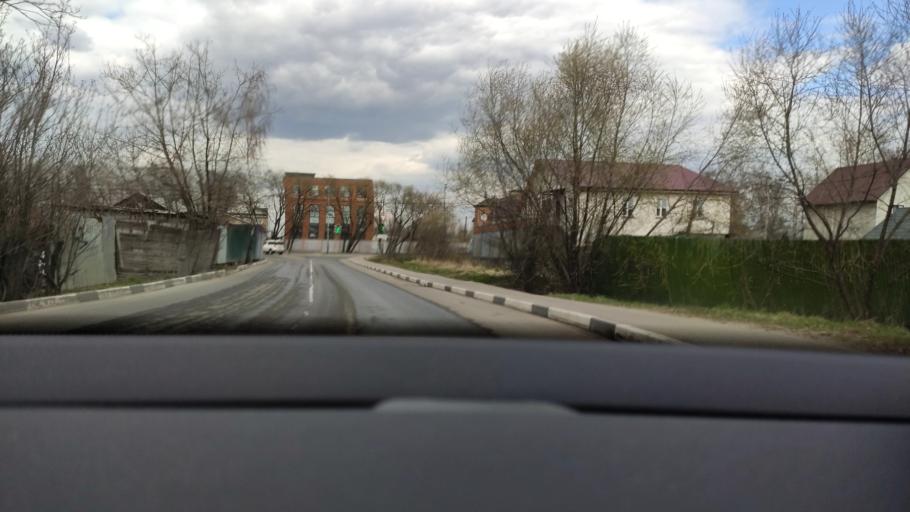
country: RU
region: Moskovskaya
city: Lesnoy Gorodok
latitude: 55.6612
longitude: 37.2381
